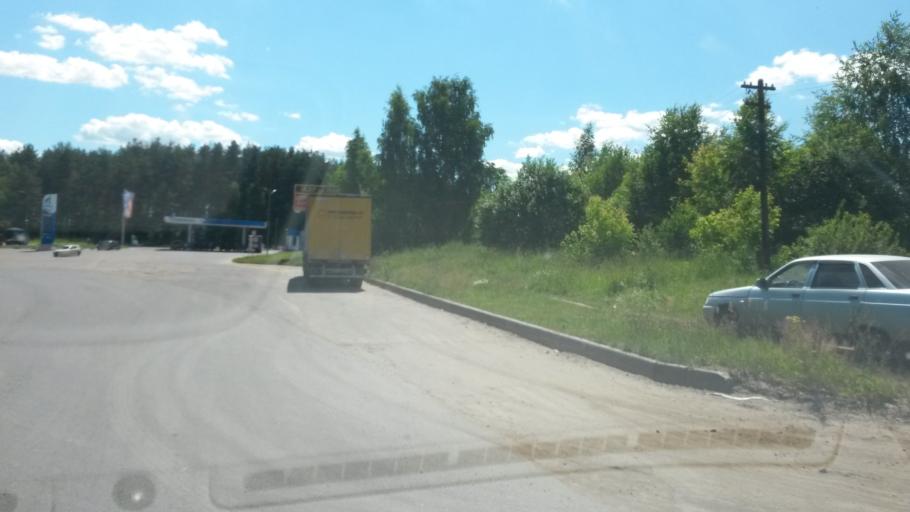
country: RU
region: Ivanovo
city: Kokhma
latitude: 56.9661
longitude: 41.0591
